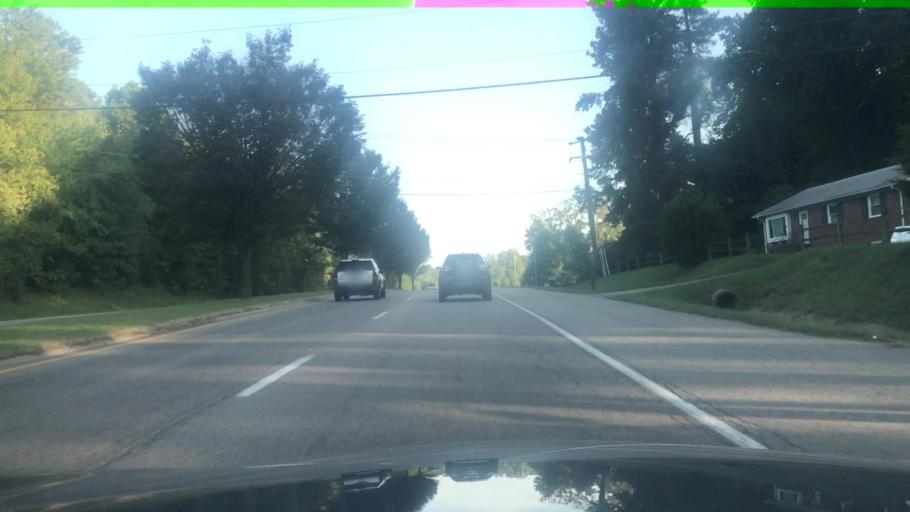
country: US
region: Virginia
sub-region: Chesterfield County
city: Brandermill
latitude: 37.4535
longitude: -77.5874
